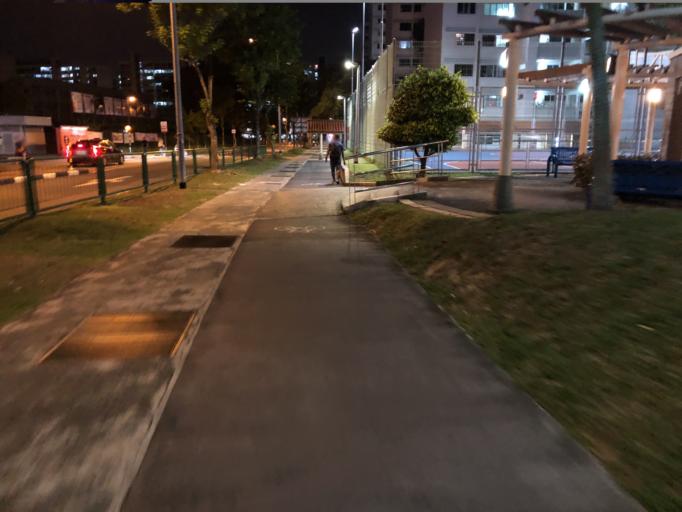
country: MY
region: Johor
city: Kampung Pasir Gudang Baru
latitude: 1.4340
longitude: 103.8365
